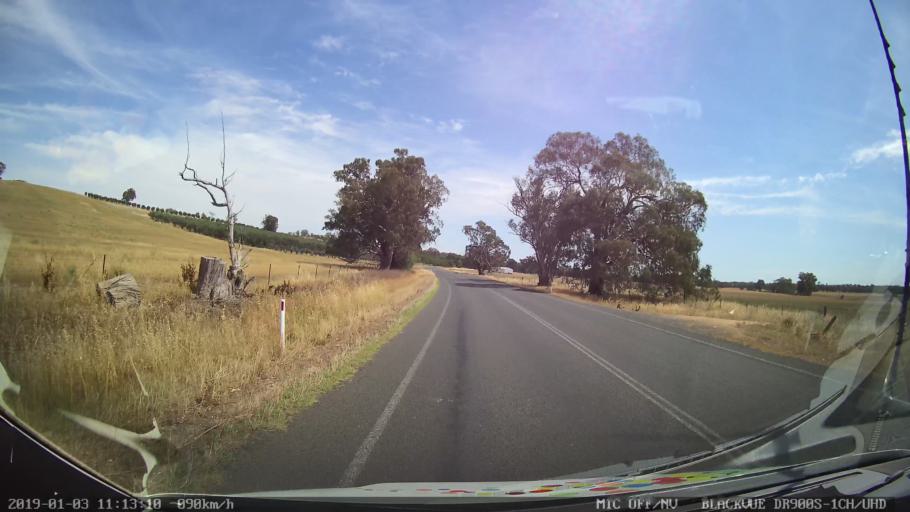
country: AU
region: New South Wales
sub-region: Young
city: Young
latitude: -34.1922
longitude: 148.2613
